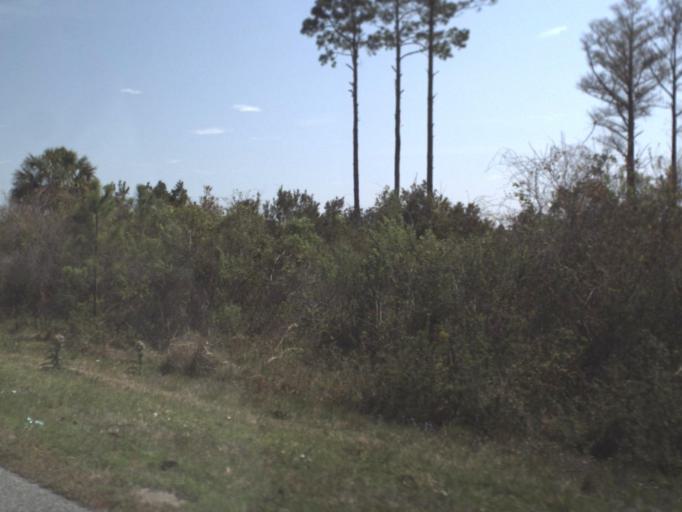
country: US
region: Florida
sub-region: Franklin County
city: Apalachicola
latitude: 29.7239
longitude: -85.0767
